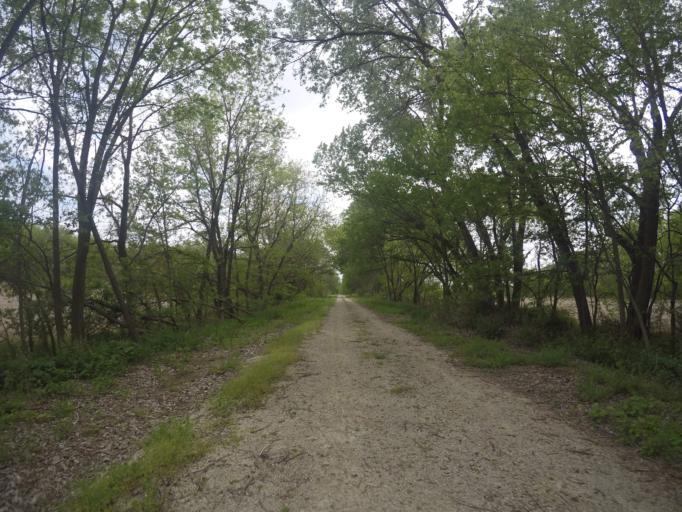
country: US
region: Nebraska
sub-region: Gage County
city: Wymore
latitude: 40.0039
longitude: -96.5942
